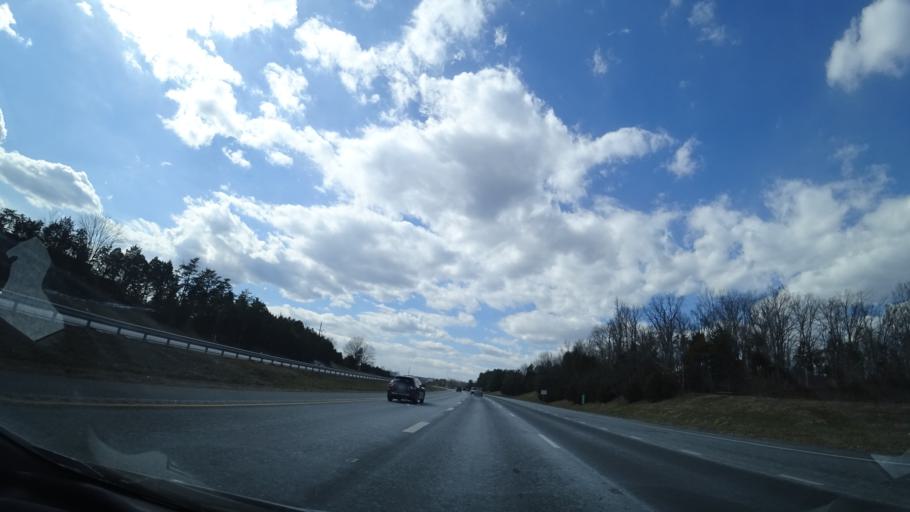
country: US
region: Virginia
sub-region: Prince William County
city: Haymarket
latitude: 38.8198
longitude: -77.6440
